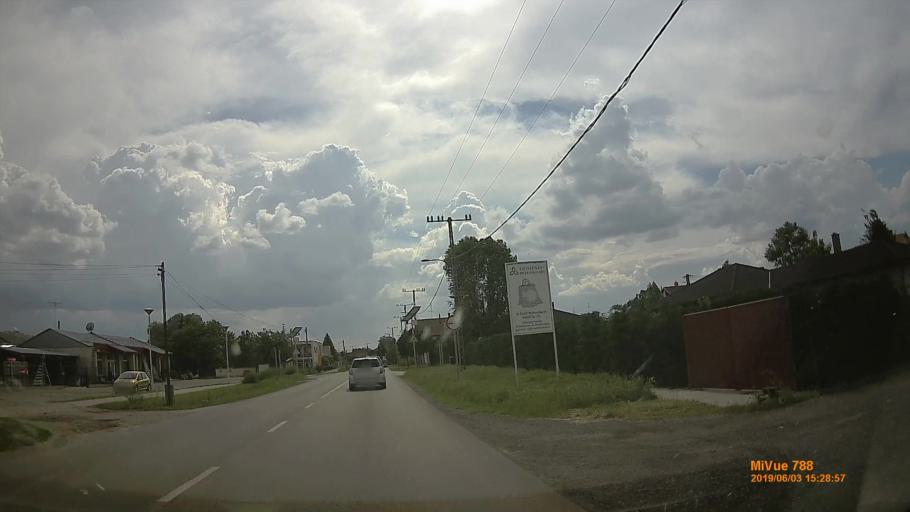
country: HU
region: Bacs-Kiskun
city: Soltvadkert
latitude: 46.5875
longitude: 19.3993
